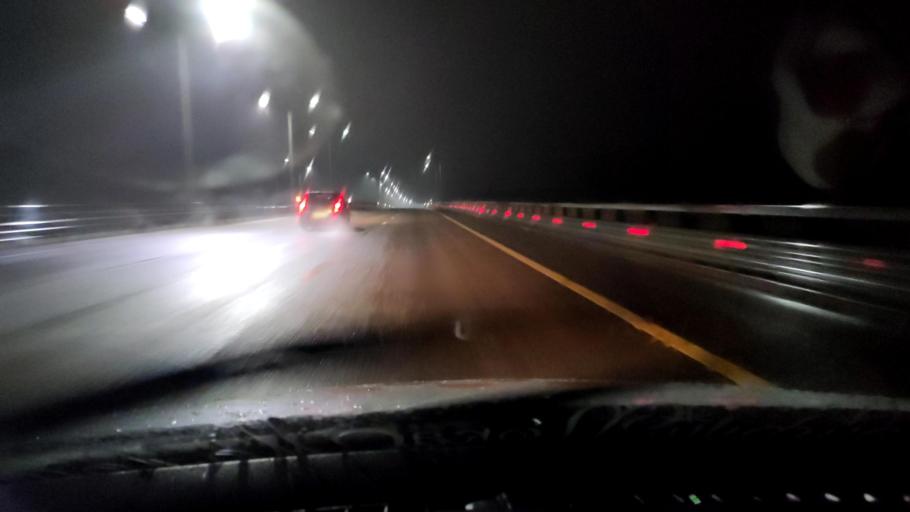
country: RU
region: Voronezj
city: Somovo
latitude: 51.7365
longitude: 39.3091
